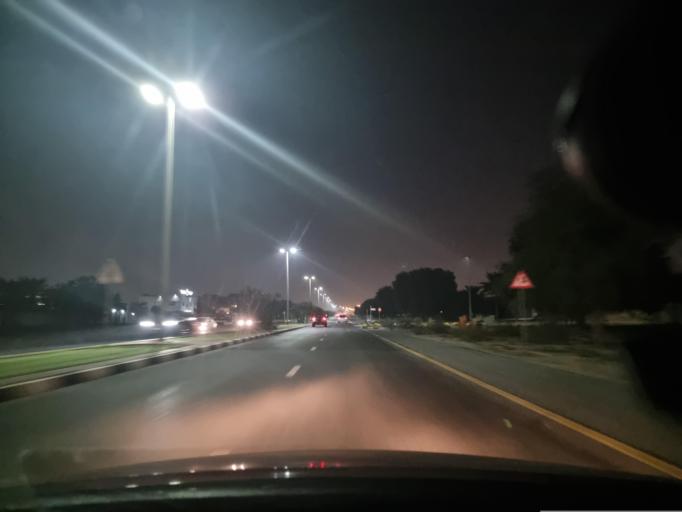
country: AE
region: Ash Shariqah
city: Sharjah
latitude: 25.3514
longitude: 55.4563
